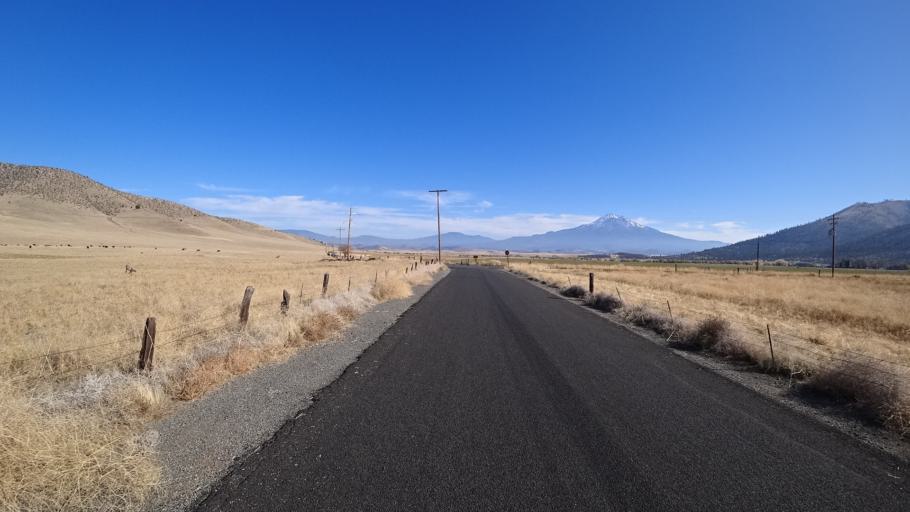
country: US
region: California
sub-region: Siskiyou County
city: Weed
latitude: 41.5035
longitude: -122.5503
